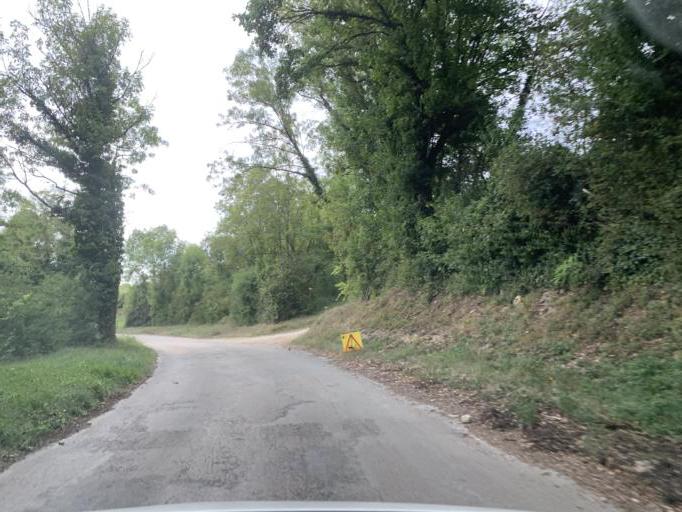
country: FR
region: Rhone-Alpes
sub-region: Departement de l'Ain
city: Vaux-en-Bugey
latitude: 45.9352
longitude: 5.3819
